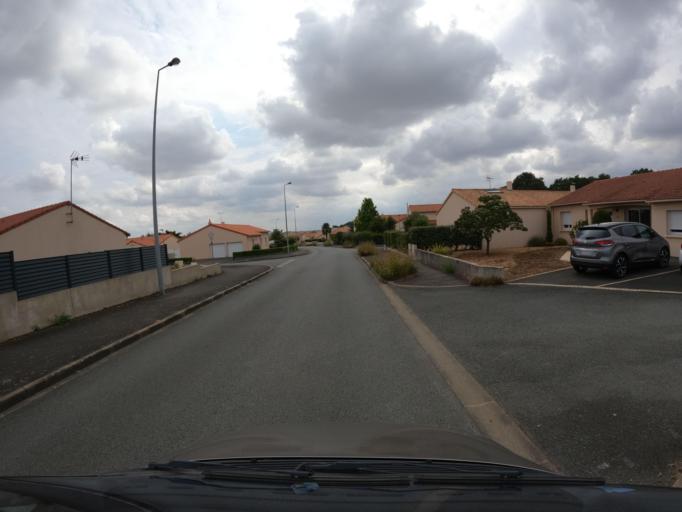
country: FR
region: Pays de la Loire
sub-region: Departement de Maine-et-Loire
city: La Seguiniere
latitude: 47.0685
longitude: -0.9440
